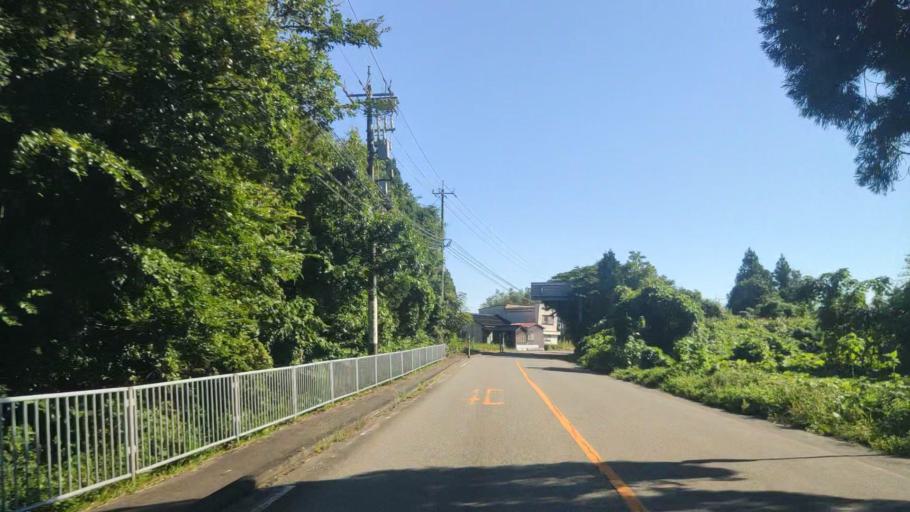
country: JP
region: Ishikawa
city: Nanao
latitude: 37.2584
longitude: 137.0893
